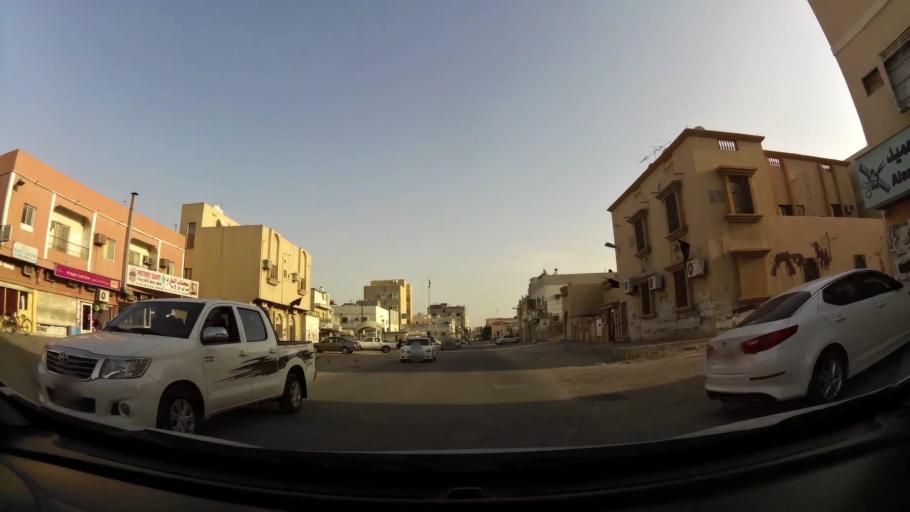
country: BH
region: Northern
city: Madinat `Isa
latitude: 26.1951
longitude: 50.4865
